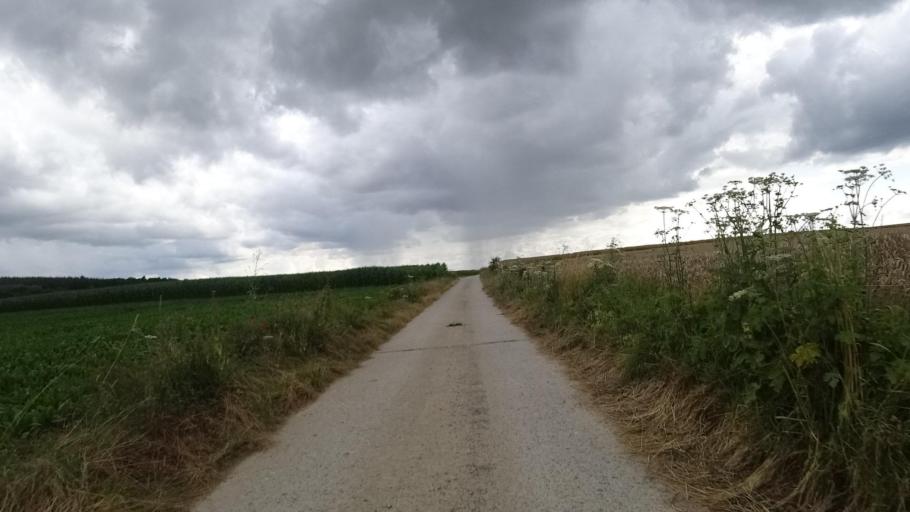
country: BE
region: Wallonia
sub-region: Province de Namur
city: Sombreffe
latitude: 50.5758
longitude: 4.5927
